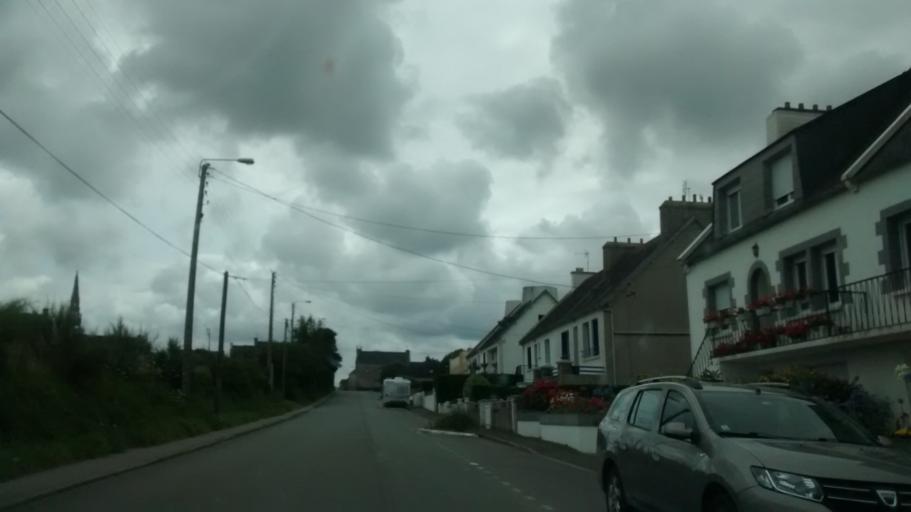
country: FR
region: Brittany
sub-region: Departement du Finistere
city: Guisseny
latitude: 48.6366
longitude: -4.4103
